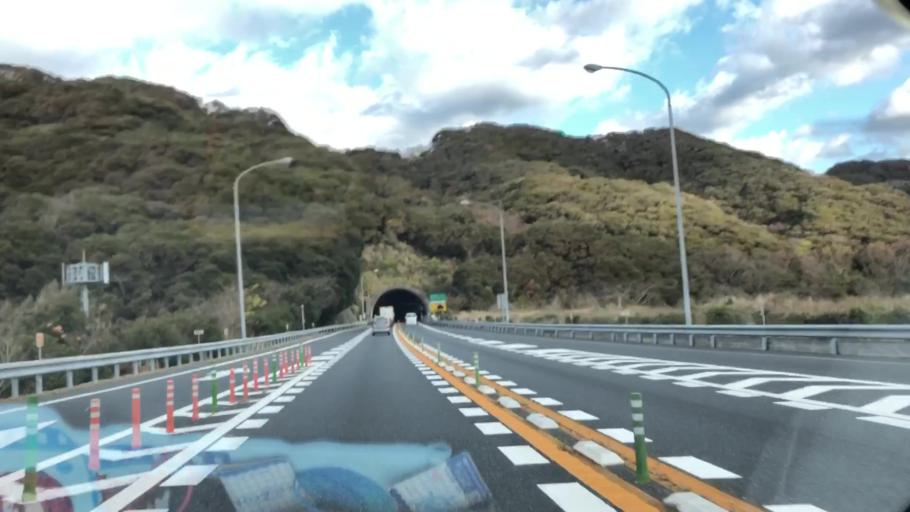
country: JP
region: Chiba
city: Futtsu
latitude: 35.1728
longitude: 139.8306
